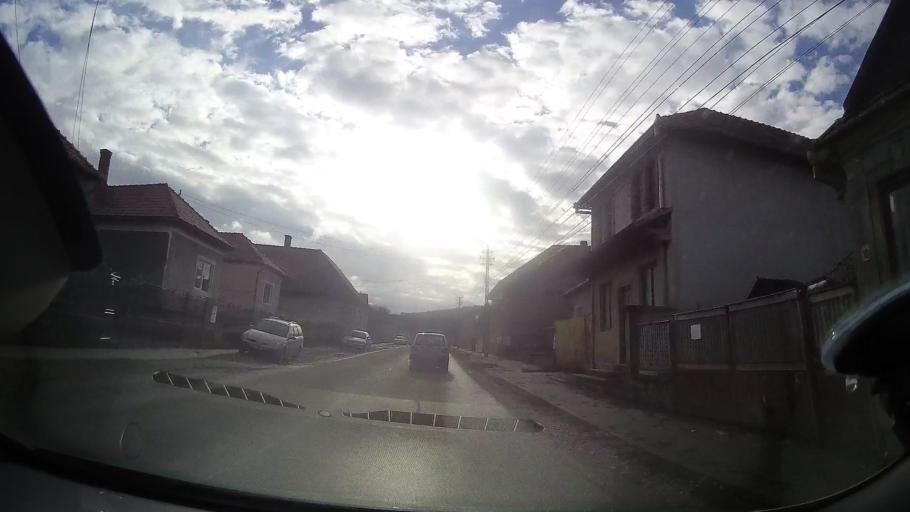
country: RO
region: Cluj
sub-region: Comuna Savadisla
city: Savadisla
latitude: 46.6768
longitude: 23.4565
